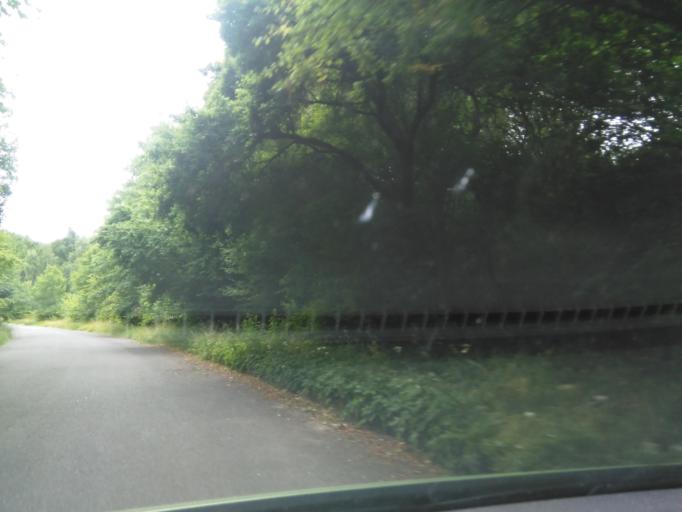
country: DK
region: Central Jutland
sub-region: Horsens Kommune
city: Horsens
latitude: 55.8711
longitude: 9.8892
